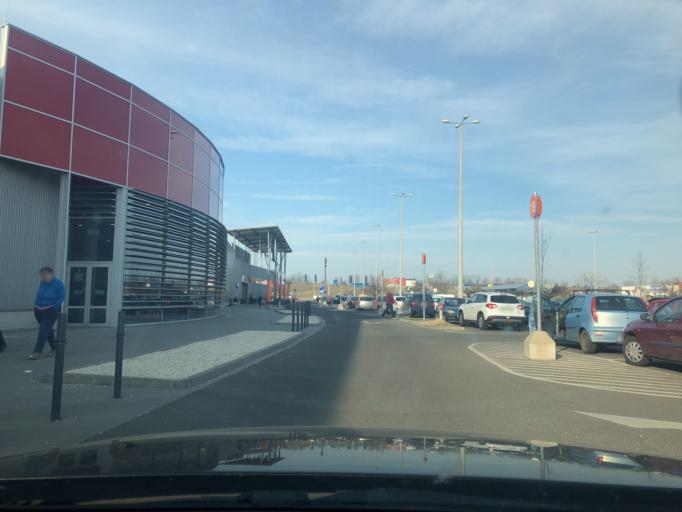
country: HU
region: Pest
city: Ecser
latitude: 47.4593
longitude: 19.3333
